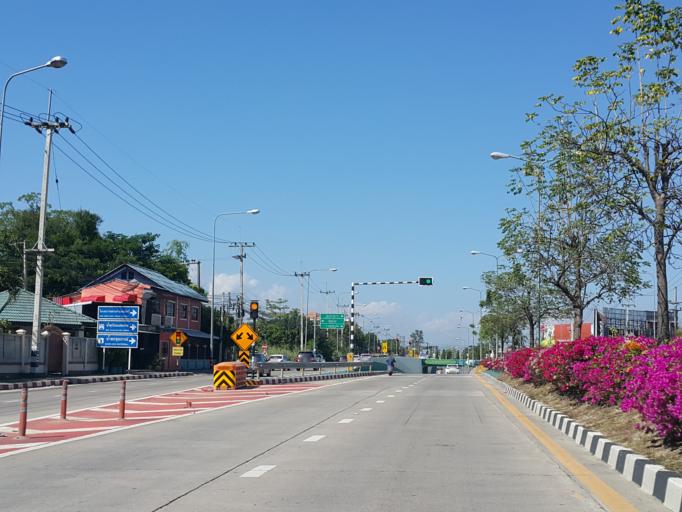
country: TH
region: Chiang Mai
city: San Sai
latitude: 18.8075
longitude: 99.0279
